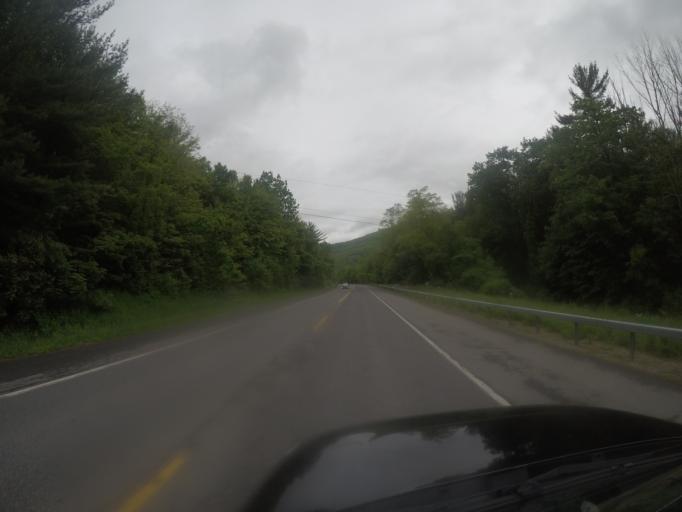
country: US
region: New York
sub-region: Ulster County
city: Shokan
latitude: 42.0729
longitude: -74.3071
